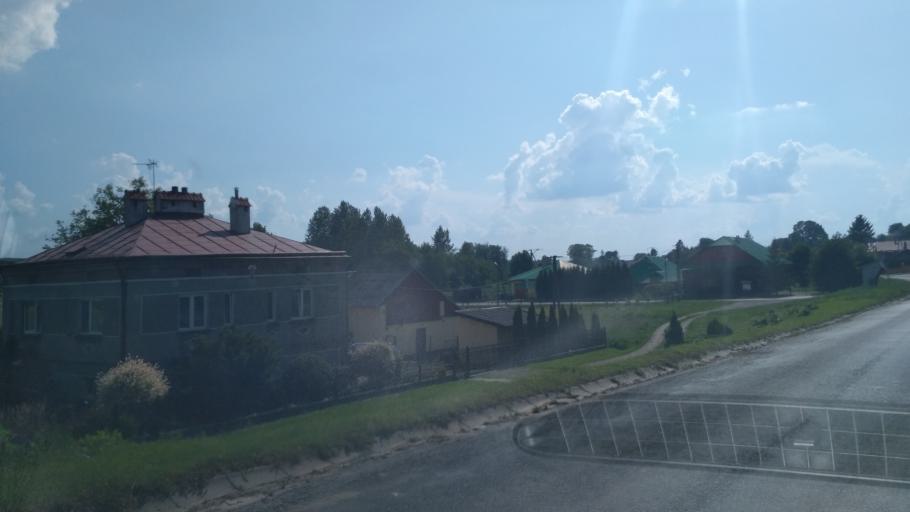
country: PL
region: Subcarpathian Voivodeship
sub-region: Powiat jaroslawski
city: Rokietnica
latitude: 49.9255
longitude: 22.6957
